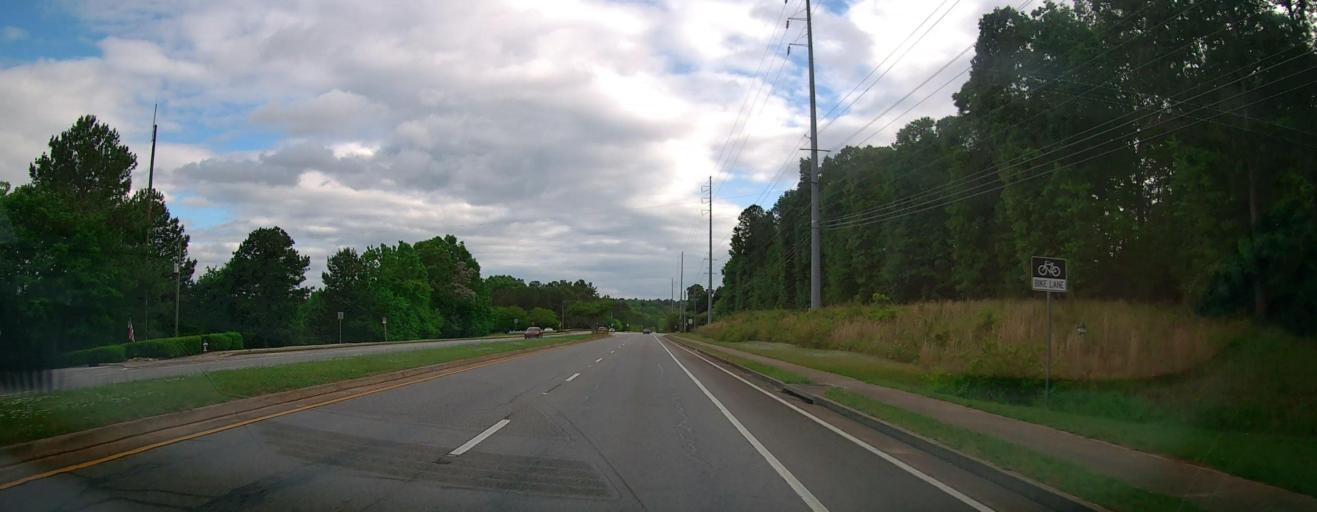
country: US
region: Georgia
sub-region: Clarke County
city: Country Club Estates
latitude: 33.9308
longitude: -83.4383
